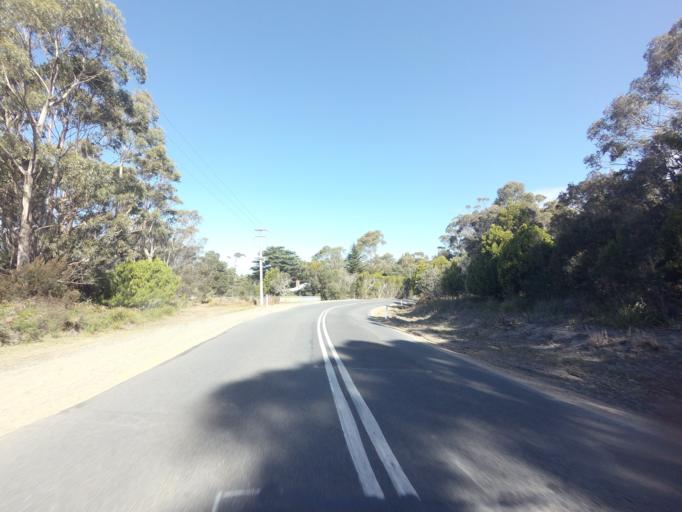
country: AU
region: Tasmania
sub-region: Break O'Day
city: St Helens
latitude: -41.6832
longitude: 148.2818
